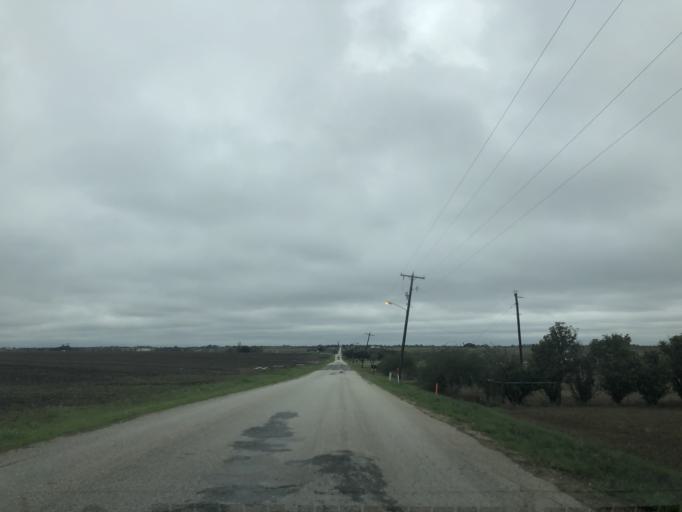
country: US
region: Texas
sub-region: Williamson County
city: Hutto
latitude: 30.5968
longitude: -97.5030
